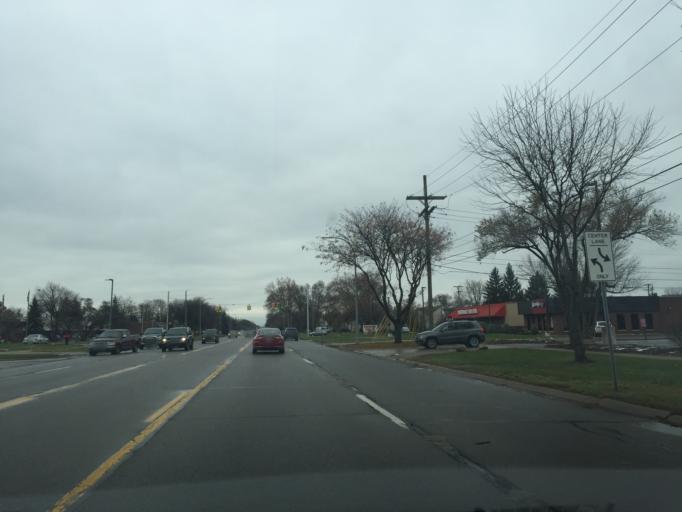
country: US
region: Michigan
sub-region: Oakland County
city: Farmington
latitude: 42.4259
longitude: -83.3359
